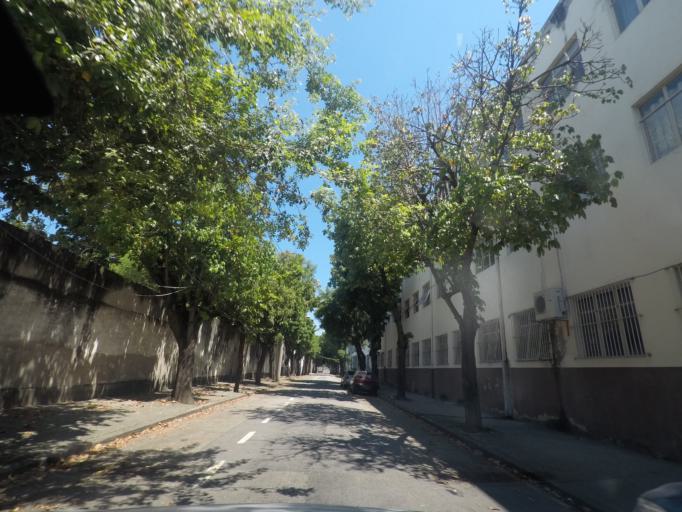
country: BR
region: Rio de Janeiro
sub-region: Rio De Janeiro
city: Rio de Janeiro
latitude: -22.9034
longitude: -43.2125
